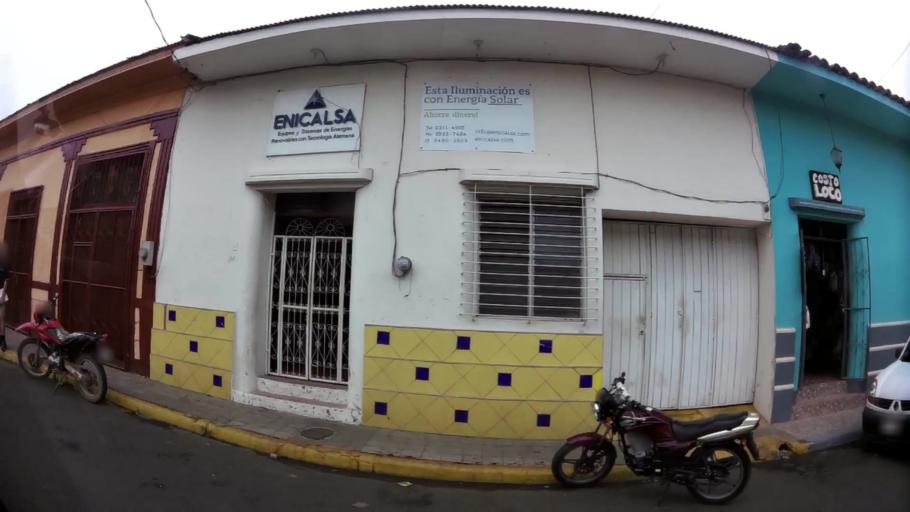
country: NI
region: Leon
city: Leon
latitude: 12.4401
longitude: -86.8759
